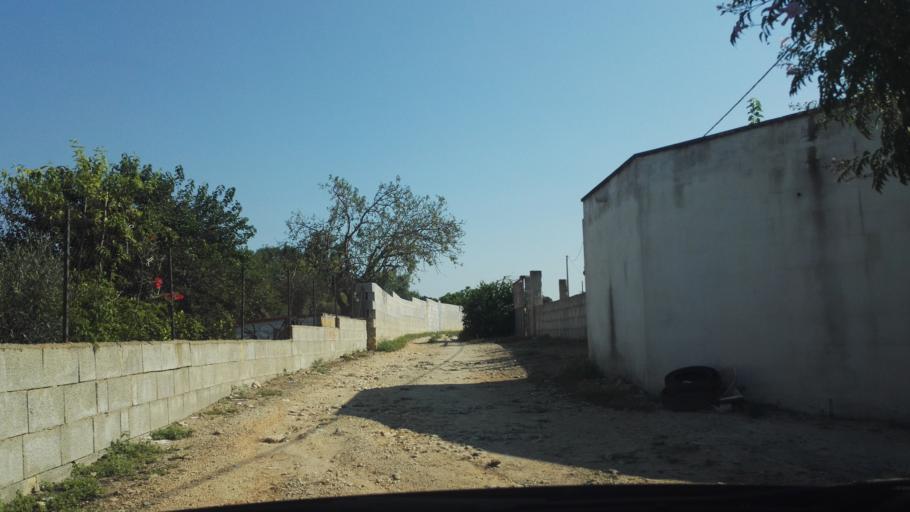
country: IT
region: Apulia
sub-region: Provincia di Lecce
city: Alezio
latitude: 40.0504
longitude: 18.0386
